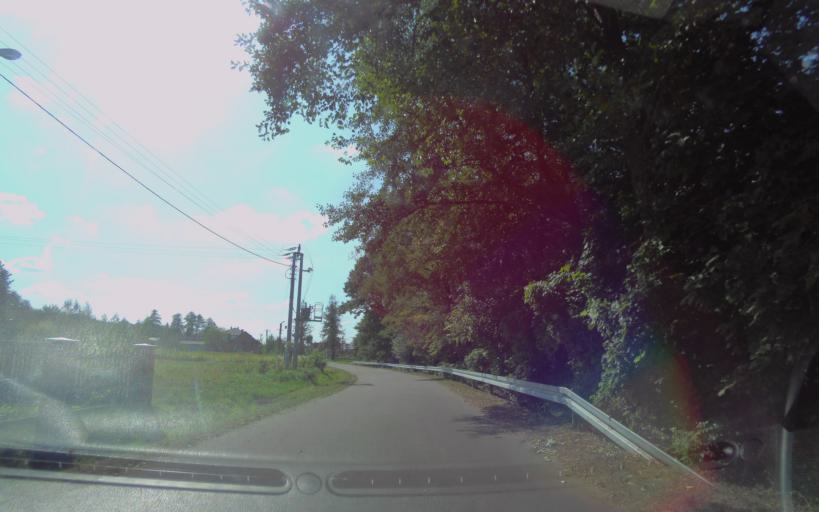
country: PL
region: Subcarpathian Voivodeship
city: Nowa Sarzyna
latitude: 50.3027
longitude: 22.3140
